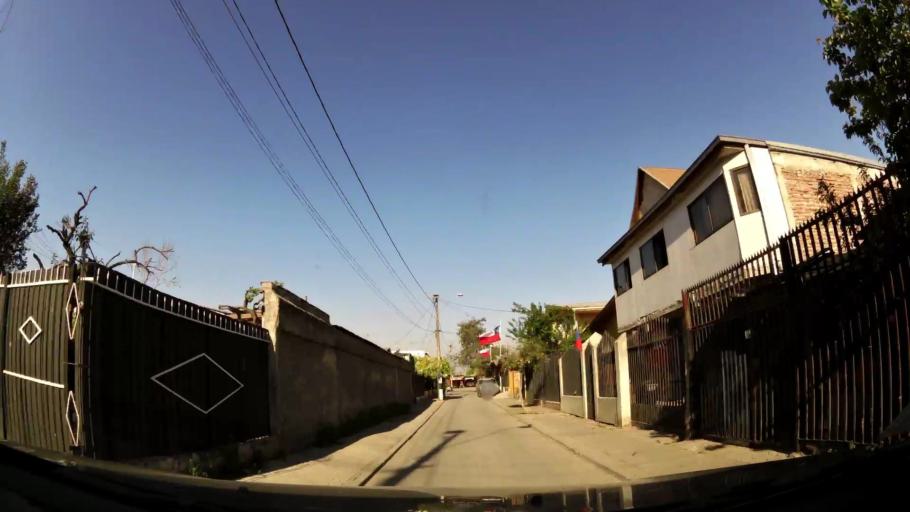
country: CL
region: Santiago Metropolitan
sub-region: Provincia de Santiago
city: La Pintana
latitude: -33.5833
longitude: -70.6613
